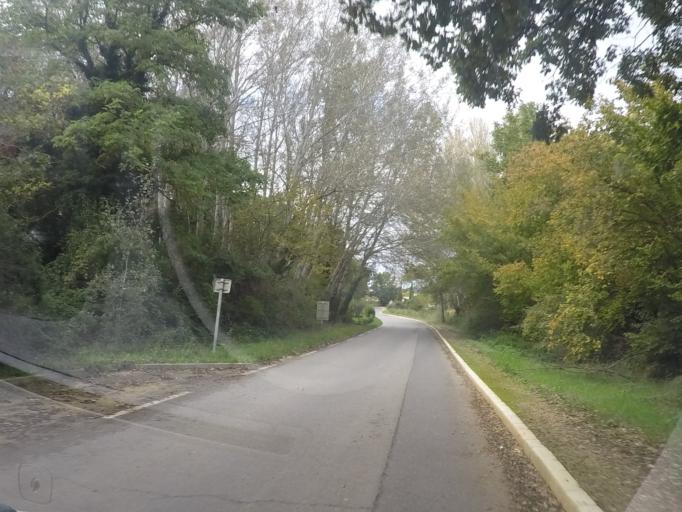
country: FR
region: Provence-Alpes-Cote d'Azur
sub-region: Departement du Vaucluse
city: Ansouis
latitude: 43.7396
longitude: 5.4609
